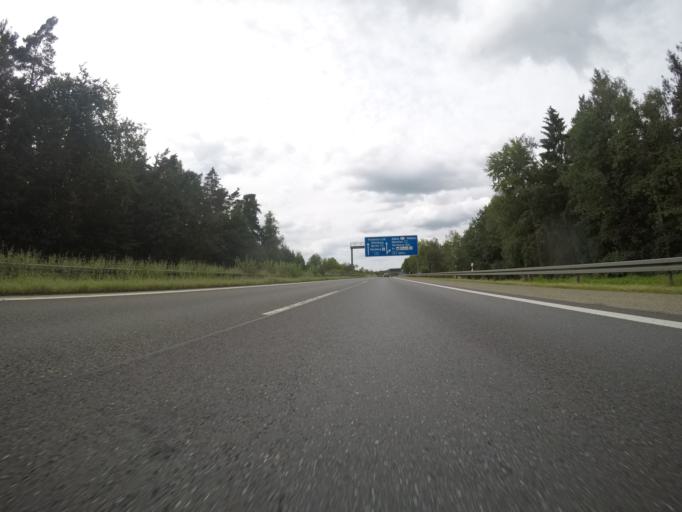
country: DE
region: Bavaria
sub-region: Regierungsbezirk Mittelfranken
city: Winkelhaid
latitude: 49.3919
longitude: 11.3116
